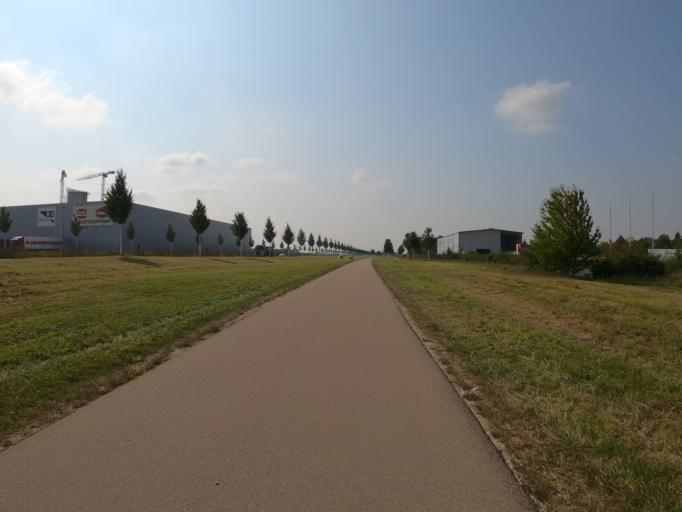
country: DE
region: Bavaria
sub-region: Swabia
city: Leipheim
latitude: 48.4406
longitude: 10.2350
